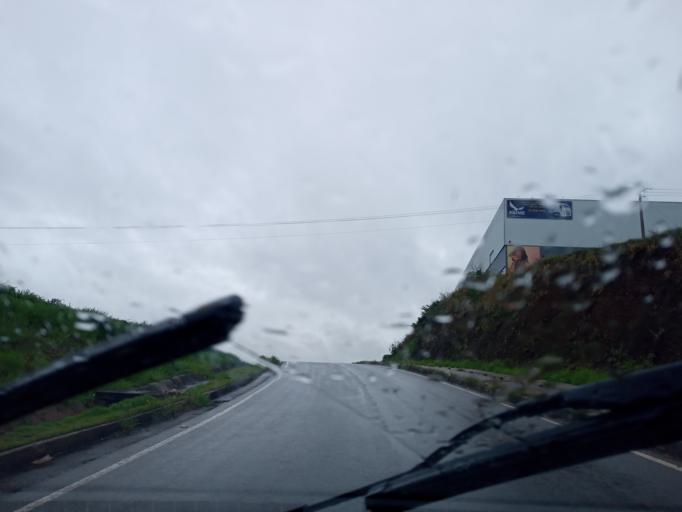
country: BR
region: Minas Gerais
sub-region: Pitangui
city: Pitangui
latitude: -19.8691
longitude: -44.9842
